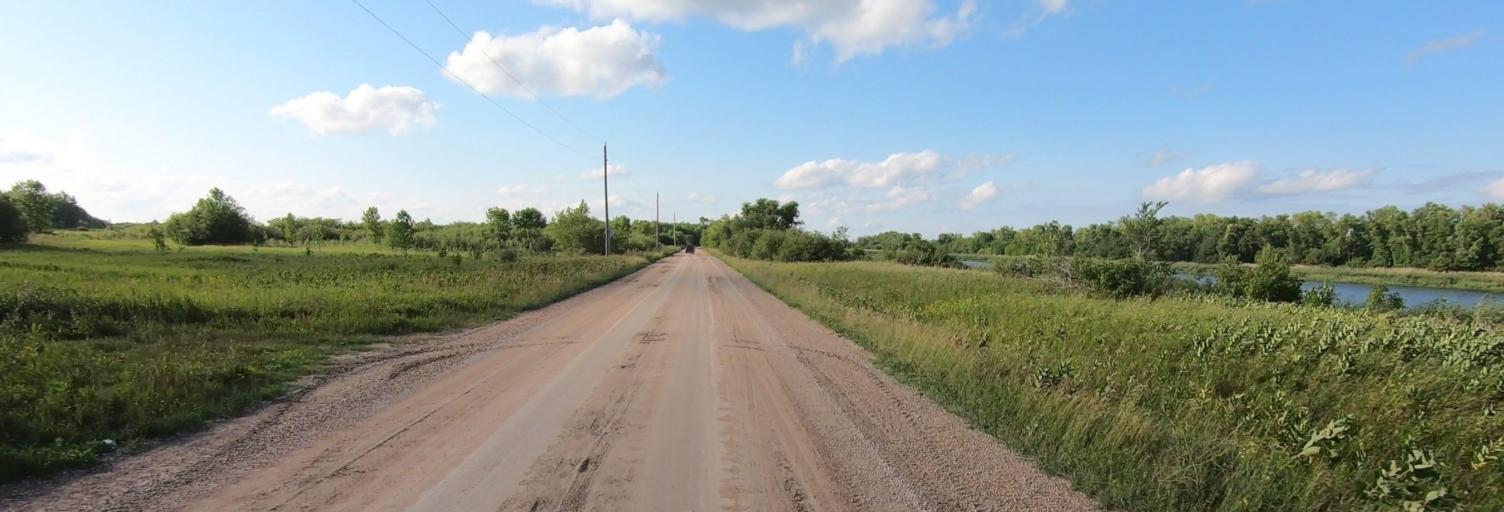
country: CA
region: Manitoba
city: Selkirk
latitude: 50.2478
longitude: -96.8456
